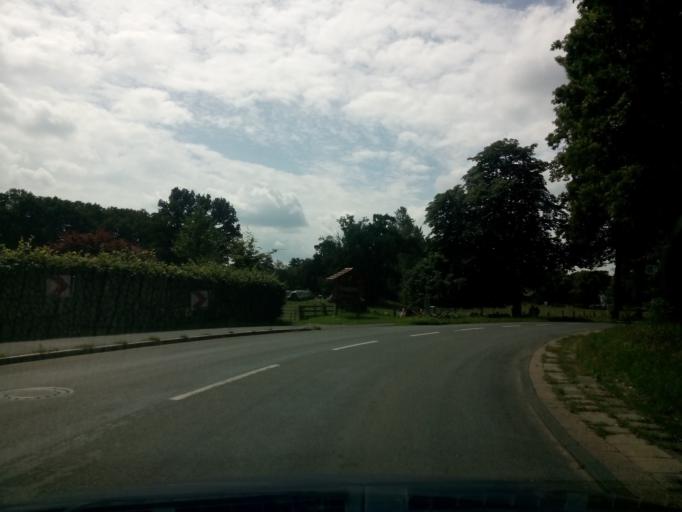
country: DE
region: Lower Saxony
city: Osterholz-Scharmbeck
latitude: 53.2479
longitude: 8.8167
